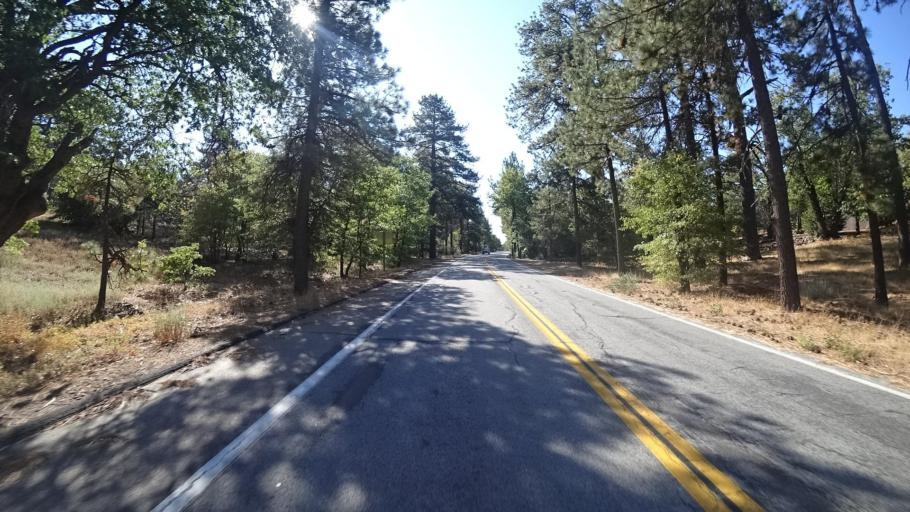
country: US
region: California
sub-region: San Diego County
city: Pine Valley
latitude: 32.8743
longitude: -116.4177
